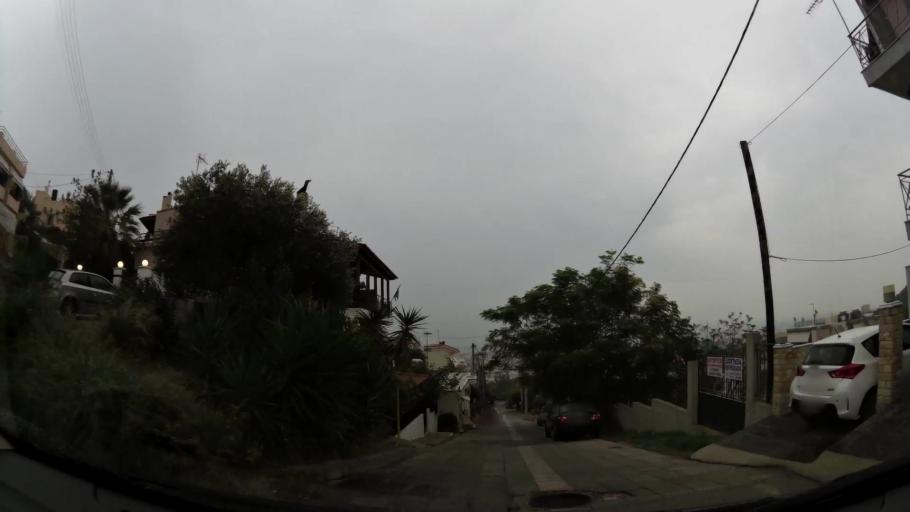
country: GR
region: Attica
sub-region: Nomarchia Athinas
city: Chaidari
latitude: 38.0057
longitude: 23.6553
